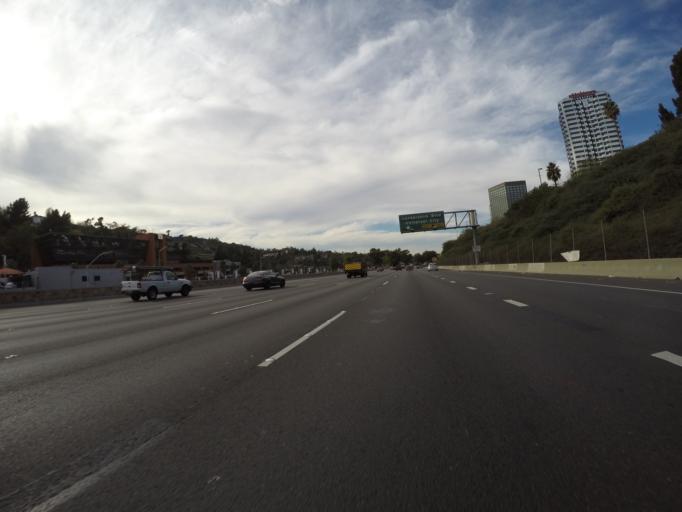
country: US
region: California
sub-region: Los Angeles County
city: Universal City
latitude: 34.1346
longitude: -118.3564
